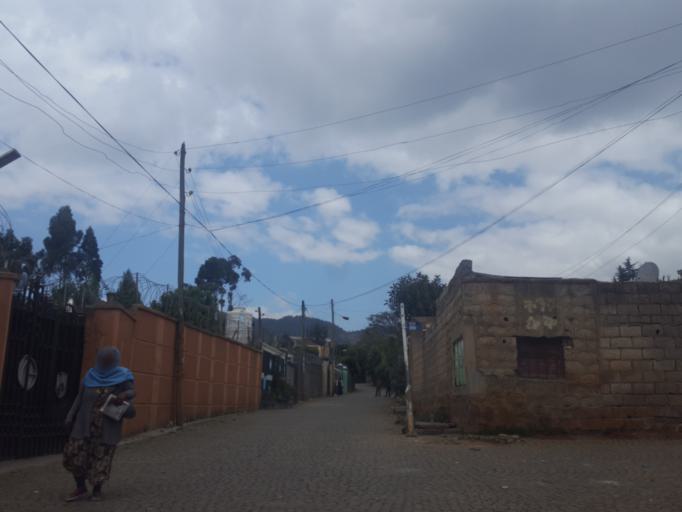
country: ET
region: Adis Abeba
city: Addis Ababa
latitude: 9.0592
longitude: 38.7176
